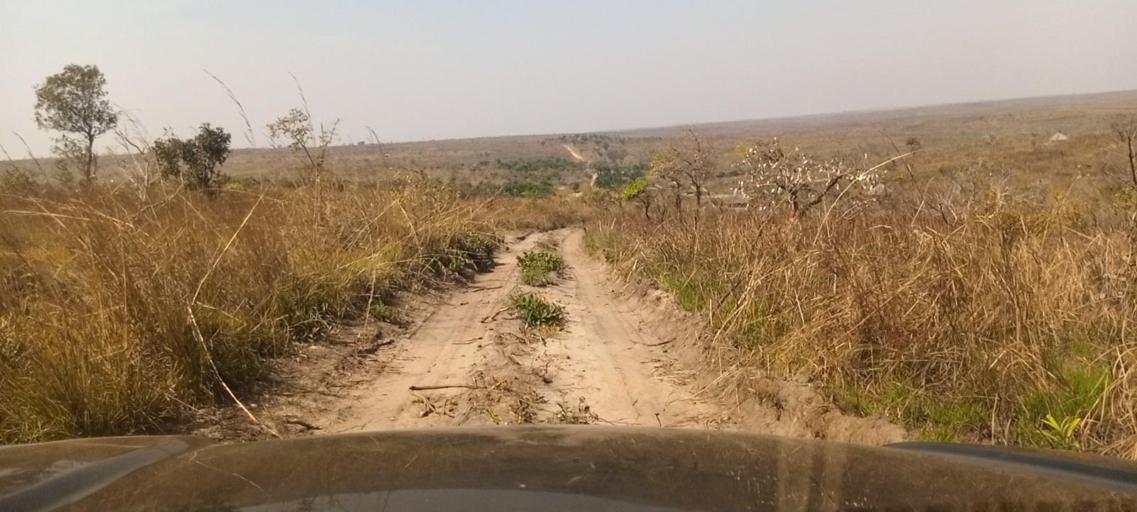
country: CD
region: Kasai-Oriental
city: Kabinda
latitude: -5.7810
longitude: 25.0543
